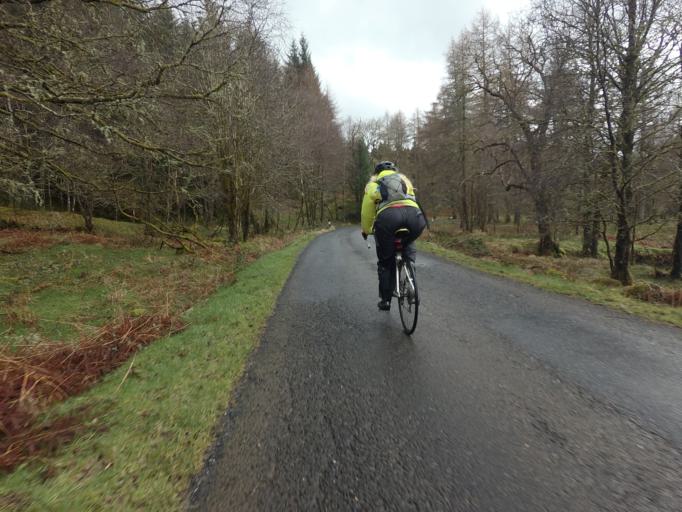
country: GB
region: Scotland
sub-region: West Dunbartonshire
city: Balloch
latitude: 56.2095
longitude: -4.5350
